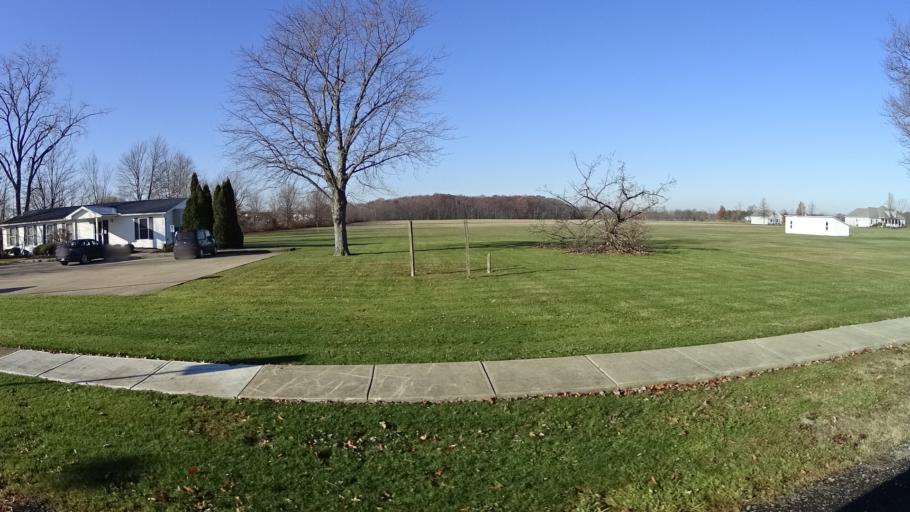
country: US
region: Ohio
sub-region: Lorain County
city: Lagrange
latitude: 41.2469
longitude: -82.1197
